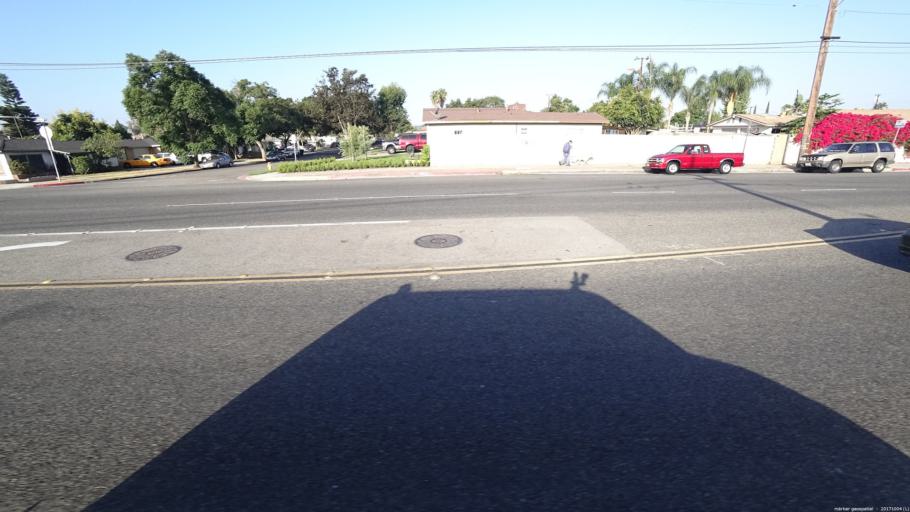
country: US
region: California
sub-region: Orange County
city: Garden Grove
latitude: 33.7913
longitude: -117.9062
